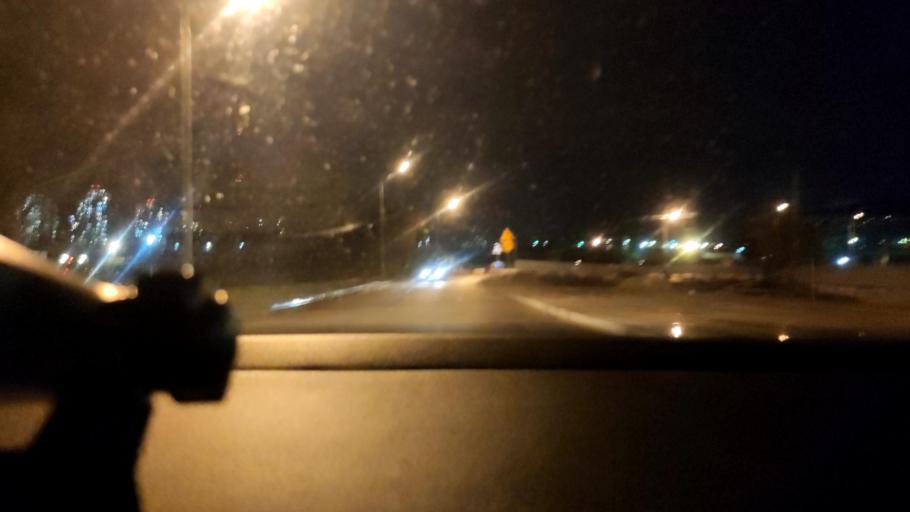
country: RU
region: Moskovskaya
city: Kur'yanovo
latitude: 55.6481
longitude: 37.6905
